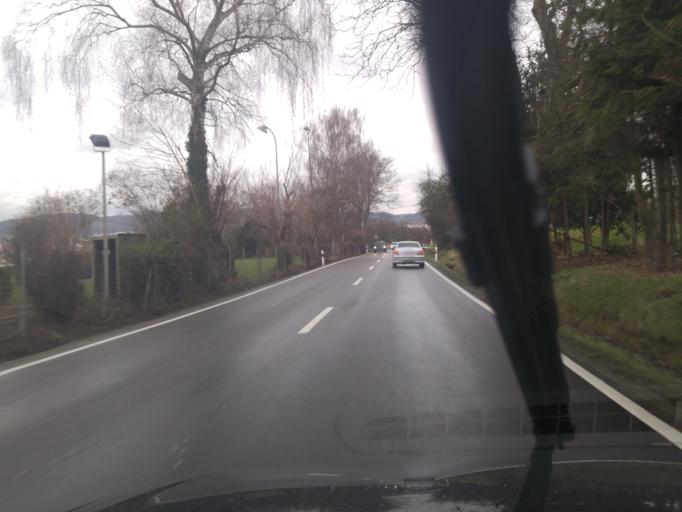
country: DE
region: Baden-Wuerttemberg
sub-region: Regierungsbezirk Stuttgart
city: Leutenbach
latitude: 48.8880
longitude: 9.3735
